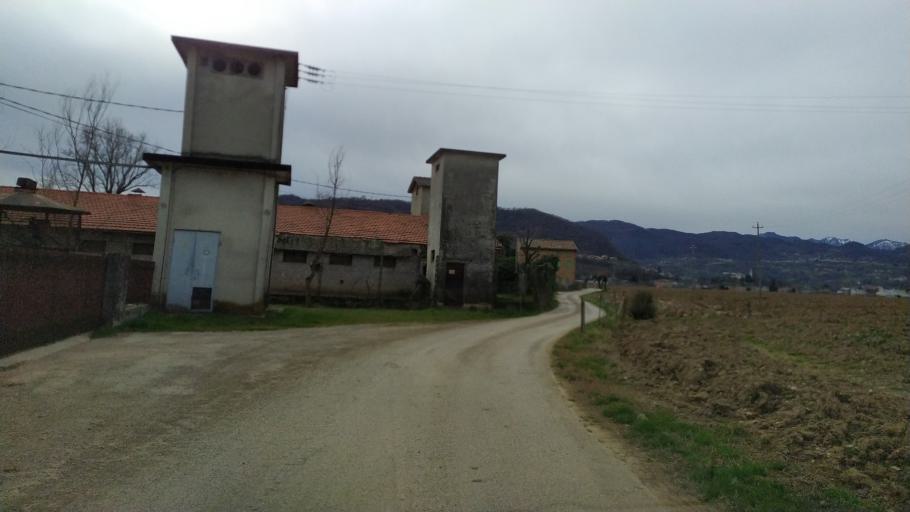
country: IT
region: Veneto
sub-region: Provincia di Vicenza
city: Malo
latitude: 45.6521
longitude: 11.4336
